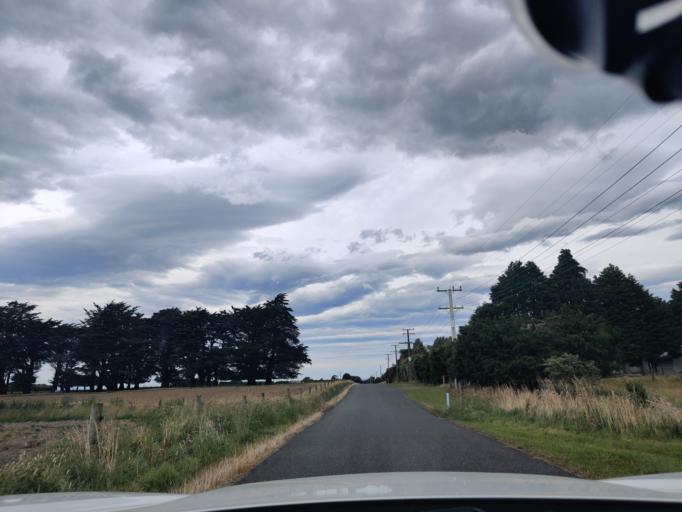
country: NZ
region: Wellington
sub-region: Masterton District
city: Masterton
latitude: -41.0367
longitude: 175.4278
